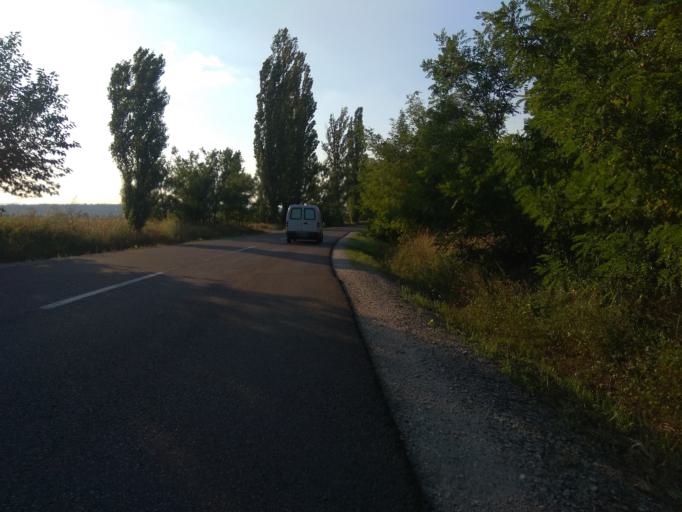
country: HU
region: Borsod-Abauj-Zemplen
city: Nyekladhaza
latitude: 47.9637
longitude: 20.8605
